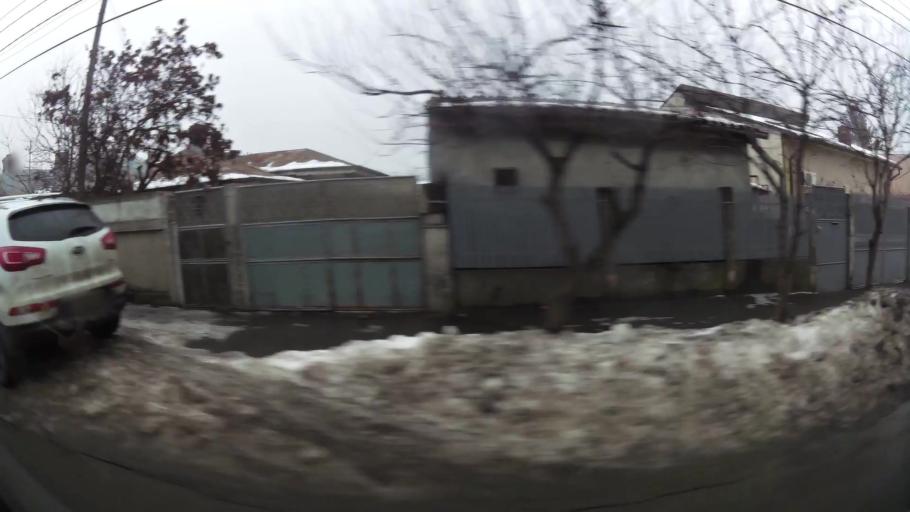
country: RO
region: Ilfov
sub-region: Comuna Chiajna
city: Chiajna
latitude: 44.4625
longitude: 25.9814
